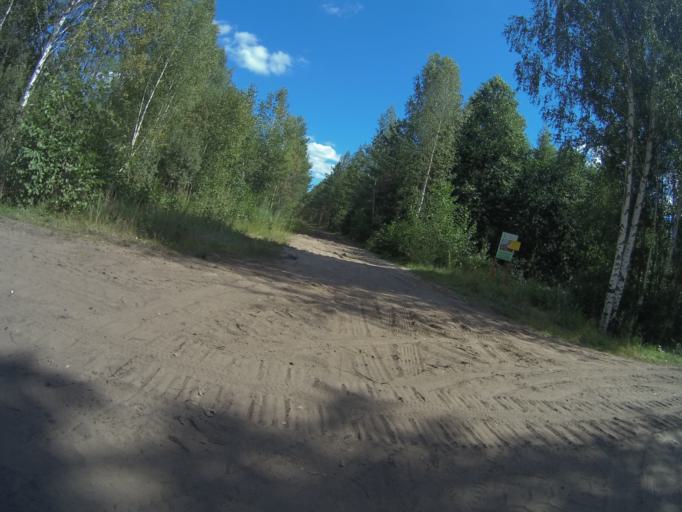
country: RU
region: Vladimir
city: Urshel'skiy
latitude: 55.7427
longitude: 40.0581
